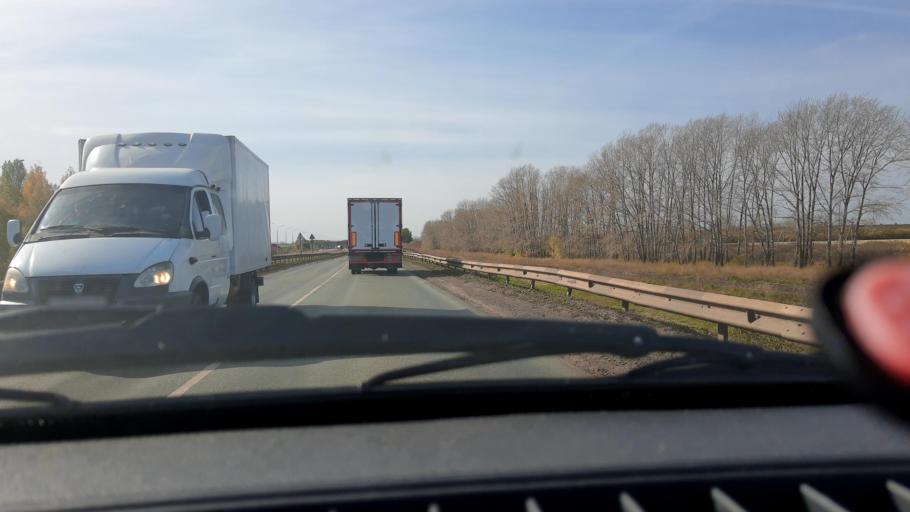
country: RU
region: Bashkortostan
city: Buzdyak
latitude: 54.6600
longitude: 54.6641
